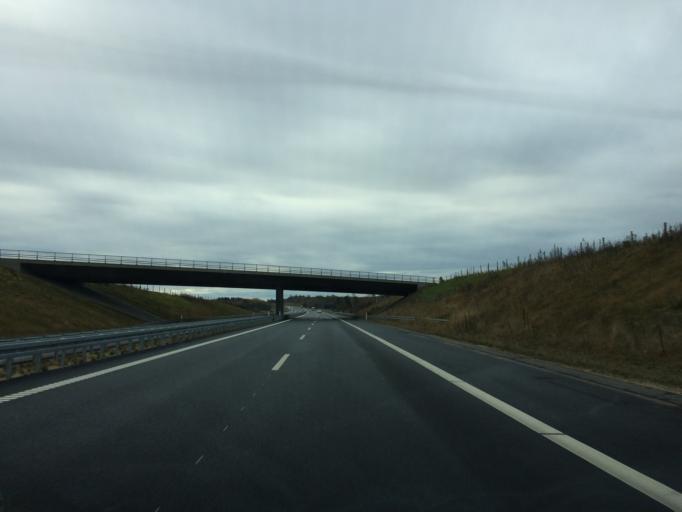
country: DK
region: Central Jutland
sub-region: Silkeborg Kommune
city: Silkeborg
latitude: 56.1908
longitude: 9.4958
